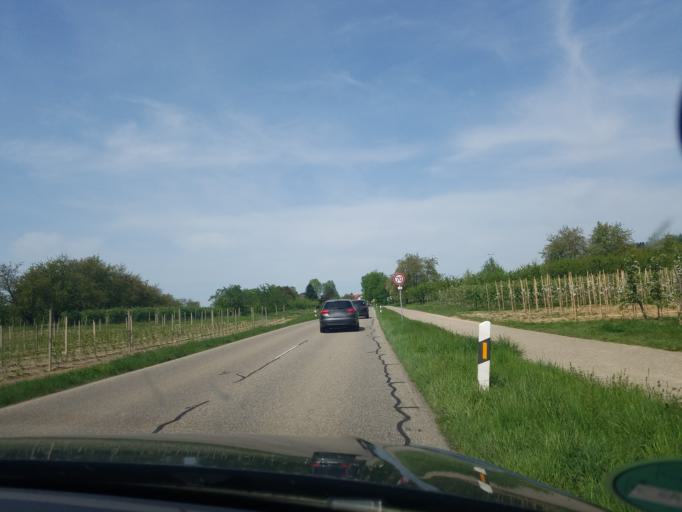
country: DE
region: Baden-Wuerttemberg
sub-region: Freiburg Region
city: Haslach
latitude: 48.5592
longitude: 8.0597
